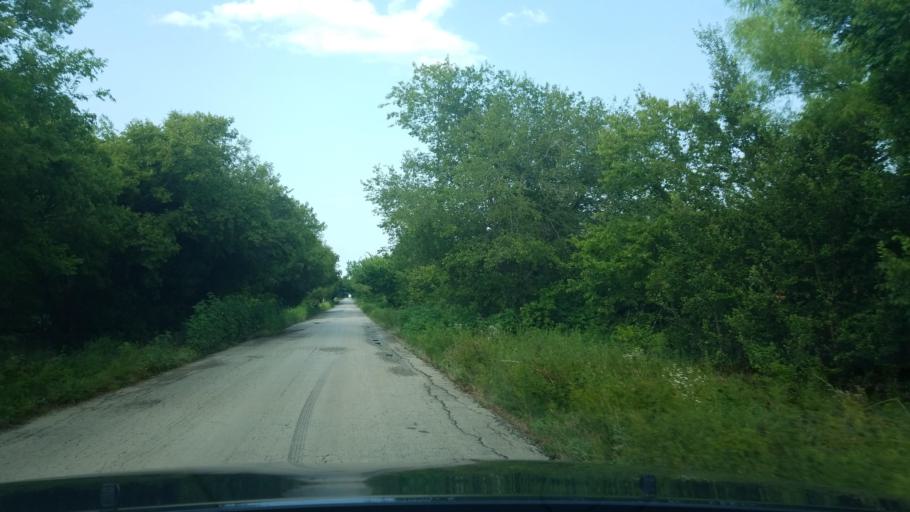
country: US
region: Texas
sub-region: Denton County
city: Denton
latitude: 33.2426
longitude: -97.0724
